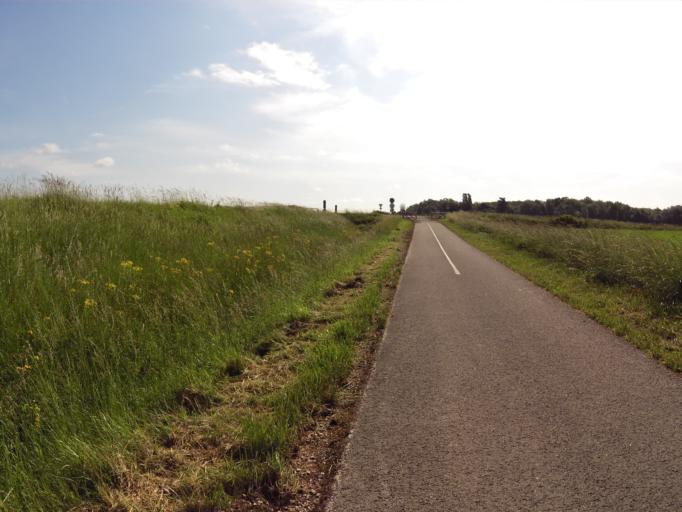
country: FR
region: Champagne-Ardenne
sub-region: Departement de l'Aube
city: Saint-Julien-les-Villas
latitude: 48.2655
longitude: 4.1269
